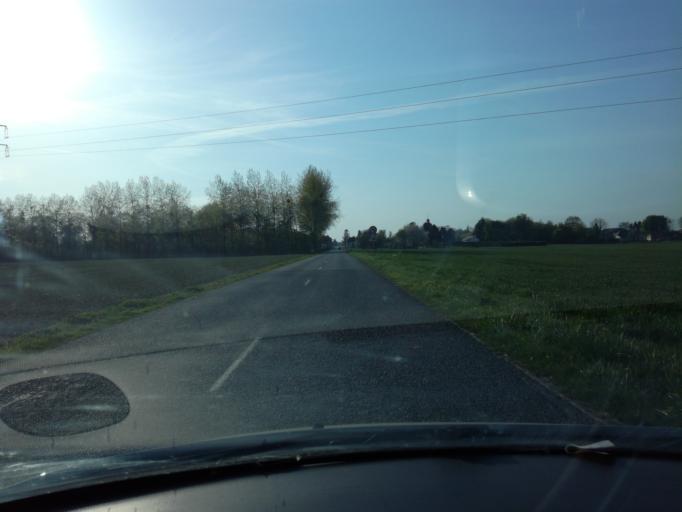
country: FR
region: Picardie
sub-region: Departement de la Somme
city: Poix-de-Picardie
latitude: 49.8232
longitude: 1.9512
